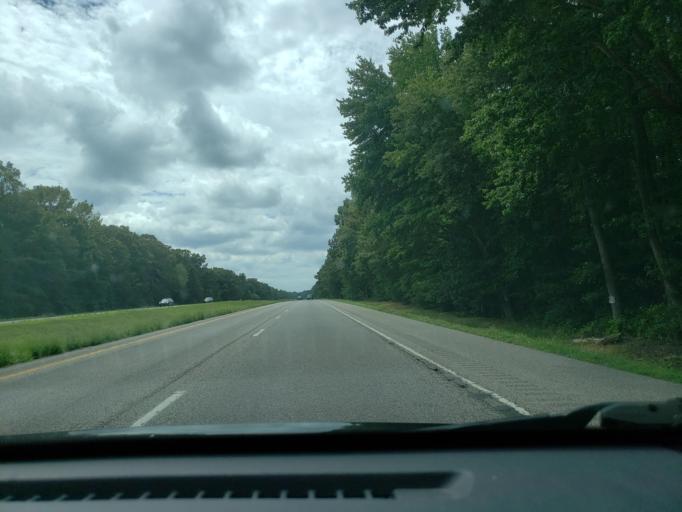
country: US
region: Delaware
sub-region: New Castle County
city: Townsend
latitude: 39.3359
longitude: -75.8368
